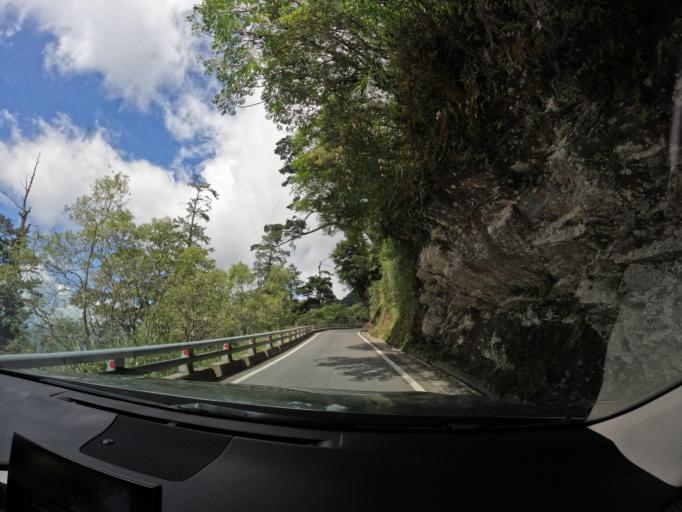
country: TW
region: Taiwan
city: Yujing
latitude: 23.2642
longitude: 120.9491
